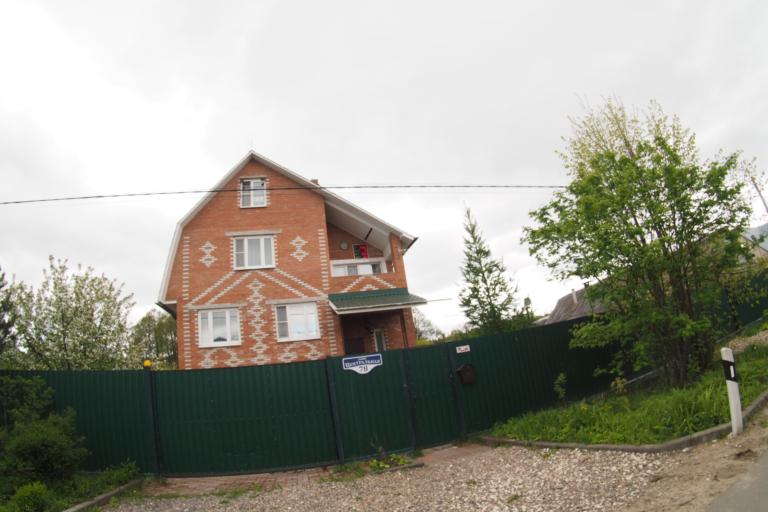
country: RU
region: Moskovskaya
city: Rechitsy
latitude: 55.5412
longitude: 38.4322
